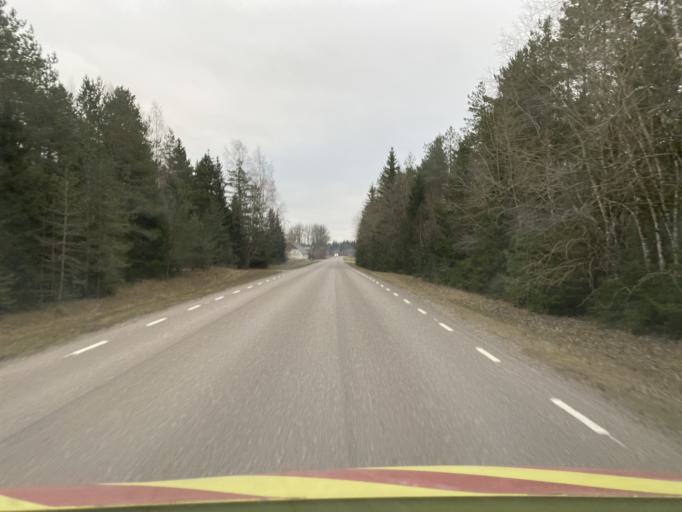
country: EE
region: Laeaene
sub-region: Ridala Parish
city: Uuemoisa
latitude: 59.0198
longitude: 23.6730
